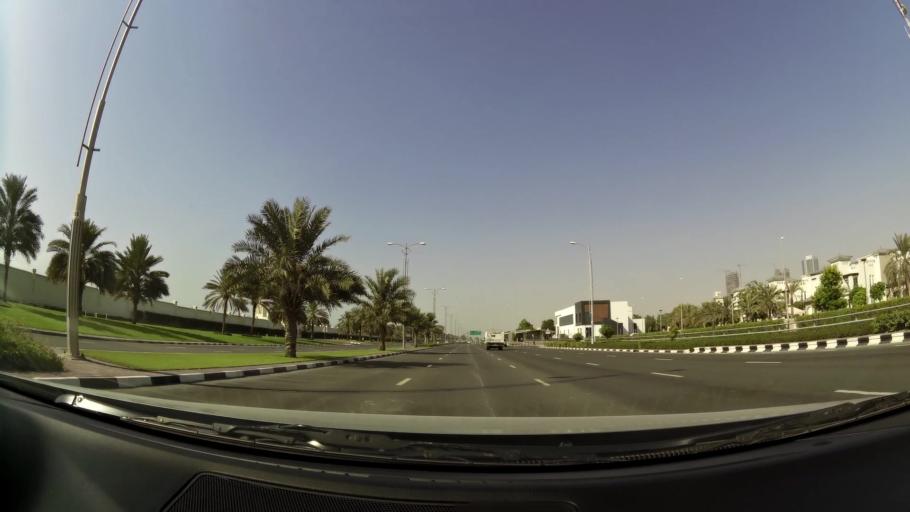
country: AE
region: Dubai
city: Dubai
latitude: 25.1071
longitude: 55.1639
